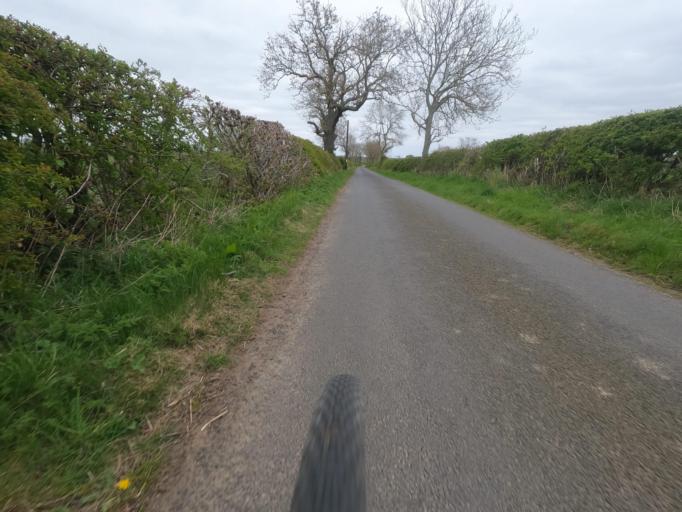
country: GB
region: England
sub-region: Northumberland
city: Meldon
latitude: 55.0761
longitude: -1.8109
